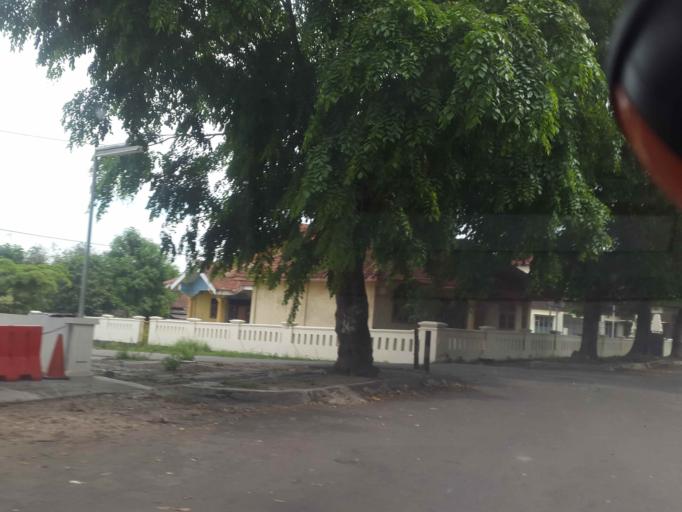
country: ID
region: Banten
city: Curug
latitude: -5.9908
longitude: 106.0480
